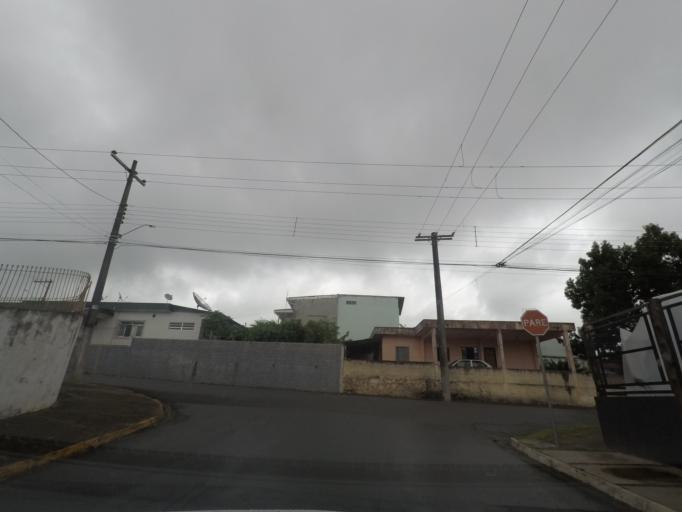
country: BR
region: Sao Paulo
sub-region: Registro
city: Registro
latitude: -24.5080
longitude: -47.8536
